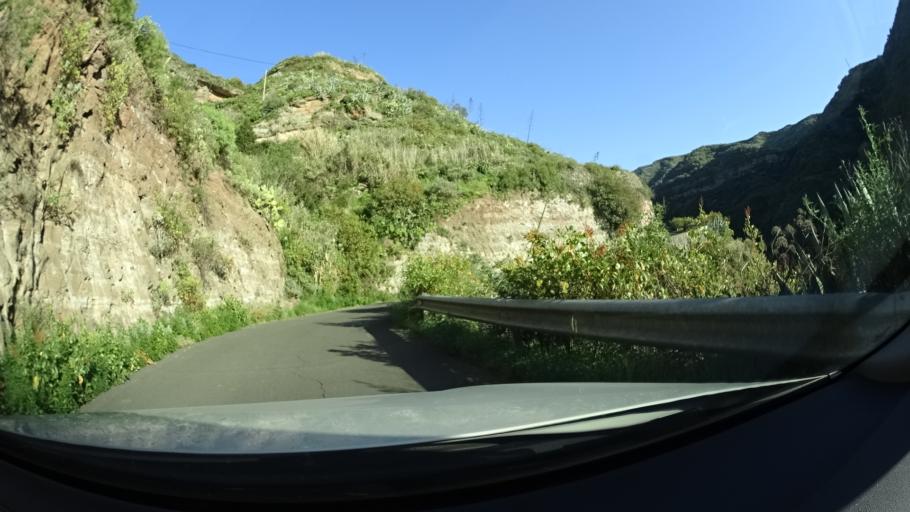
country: ES
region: Canary Islands
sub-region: Provincia de Las Palmas
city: Artenara
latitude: 28.0481
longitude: -15.6667
